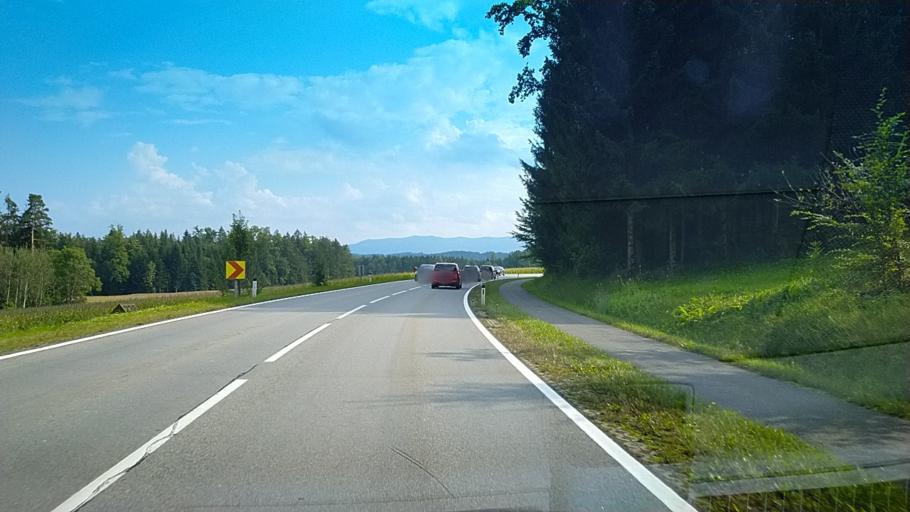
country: AT
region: Styria
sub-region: Politischer Bezirk Deutschlandsberg
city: Hollenegg
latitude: 46.7801
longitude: 15.2343
